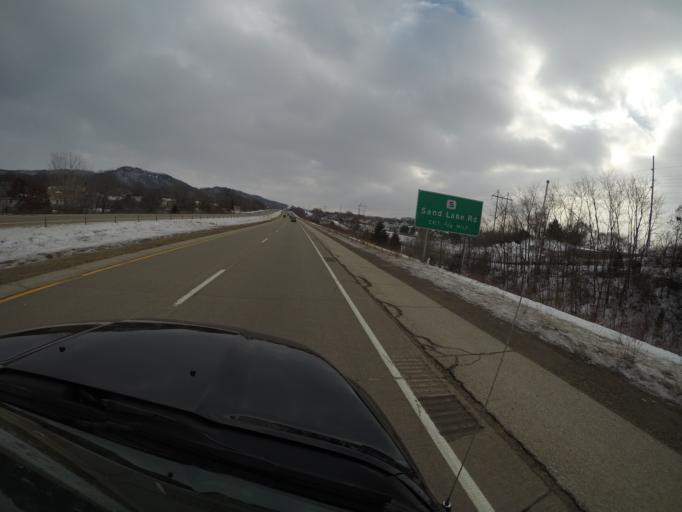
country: US
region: Wisconsin
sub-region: La Crosse County
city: Onalaska
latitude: 43.9110
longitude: -91.2339
